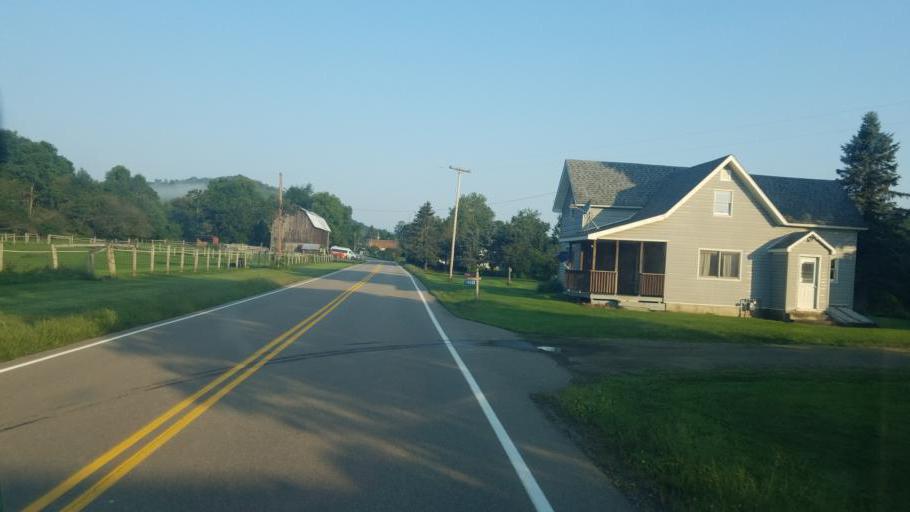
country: US
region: Pennsylvania
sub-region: Tioga County
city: Westfield
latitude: 41.9915
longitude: -77.4909
